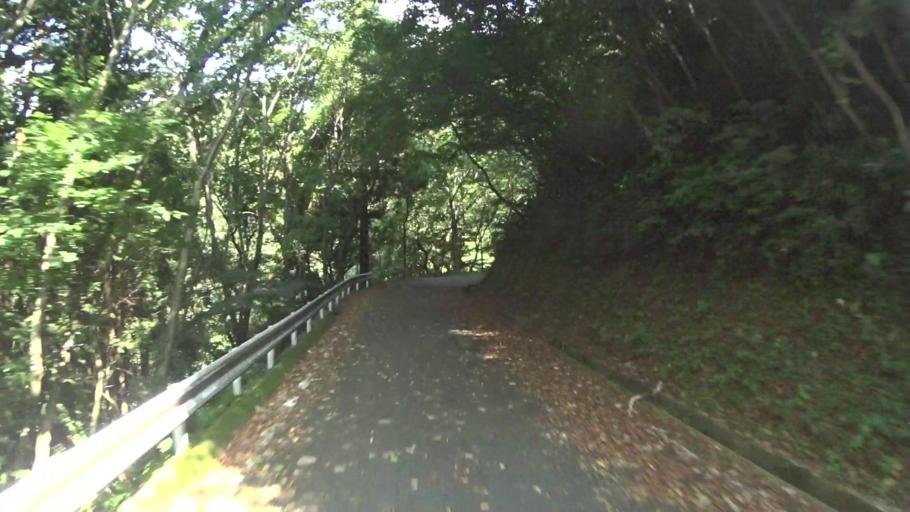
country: JP
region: Kyoto
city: Miyazu
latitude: 35.6591
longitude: 135.2349
